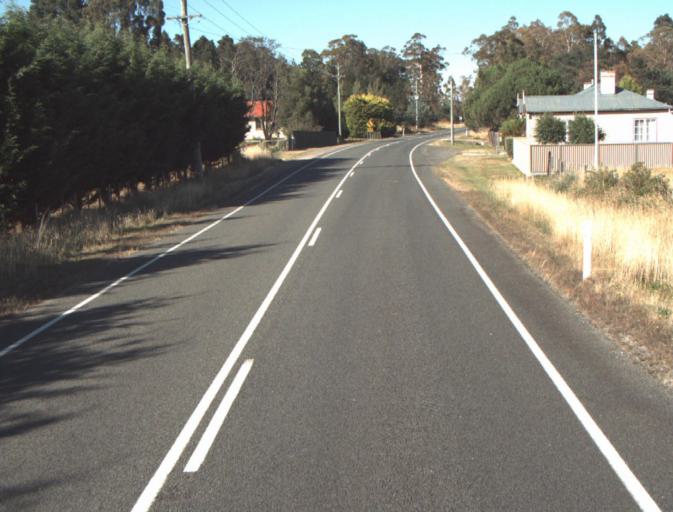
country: AU
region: Tasmania
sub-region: Launceston
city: Newstead
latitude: -41.3935
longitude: 147.2951
